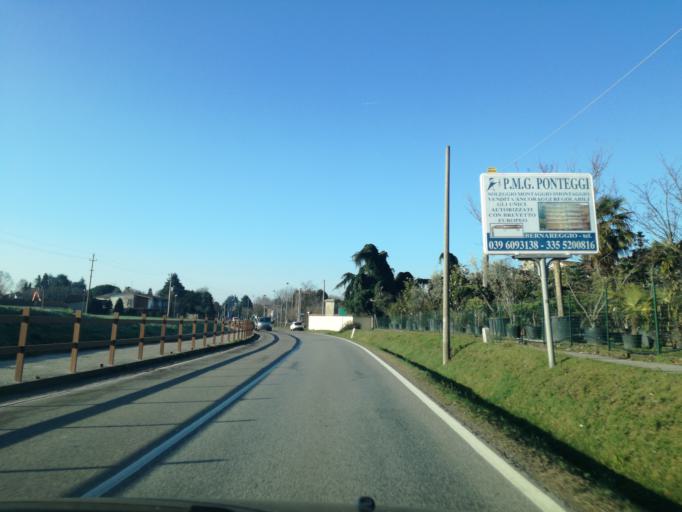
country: IT
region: Lombardy
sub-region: Provincia di Monza e Brianza
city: Villanova
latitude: 45.6300
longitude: 9.3917
